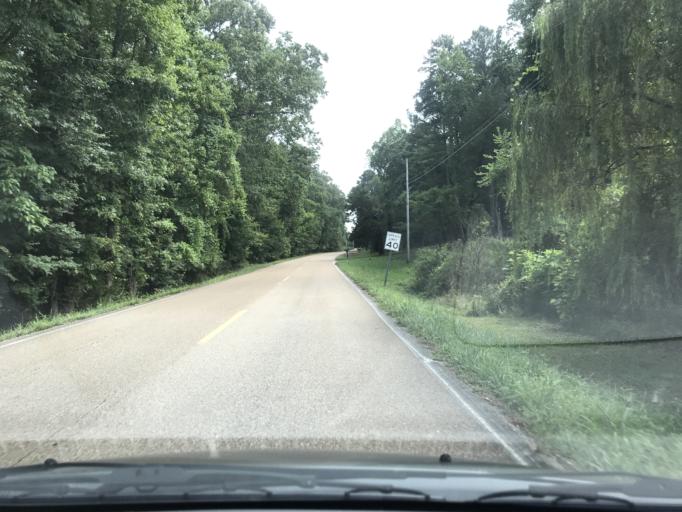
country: US
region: Tennessee
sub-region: Hamilton County
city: Lakesite
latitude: 35.1989
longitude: -85.1027
